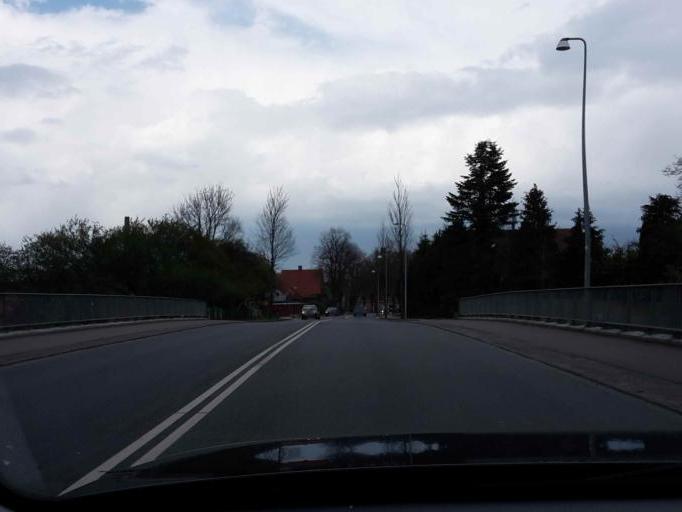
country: DK
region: South Denmark
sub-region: Odense Kommune
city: Odense
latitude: 55.3990
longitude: 10.3546
